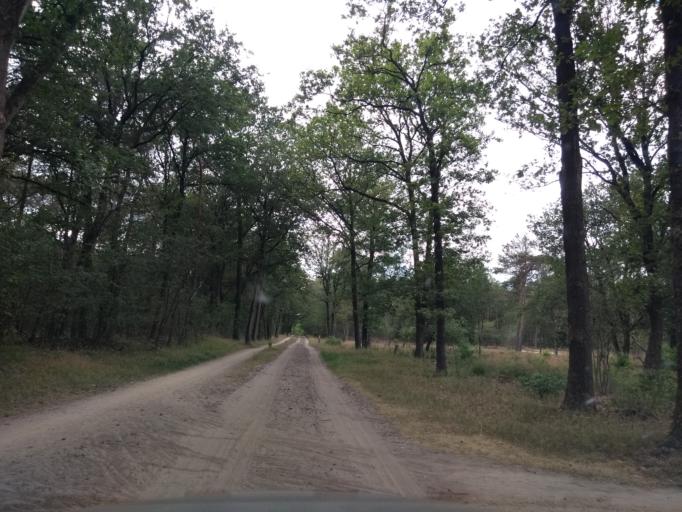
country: NL
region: Overijssel
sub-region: Gemeente Hof van Twente
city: Markelo
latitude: 52.2678
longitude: 6.4786
